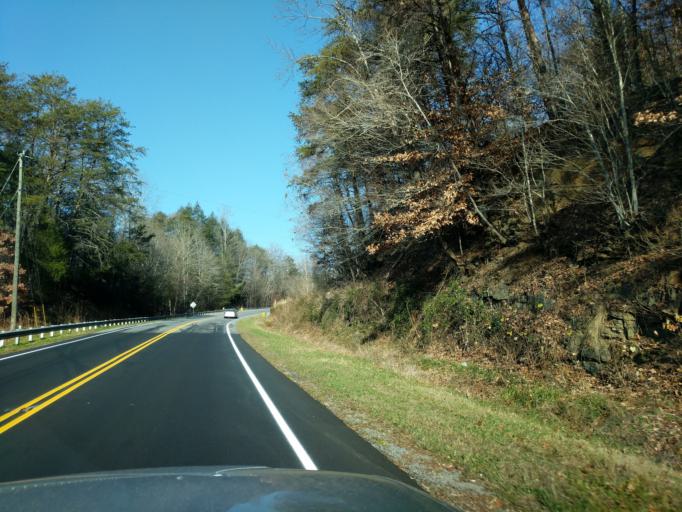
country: US
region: North Carolina
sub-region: McDowell County
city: West Marion
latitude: 35.5753
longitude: -81.9760
